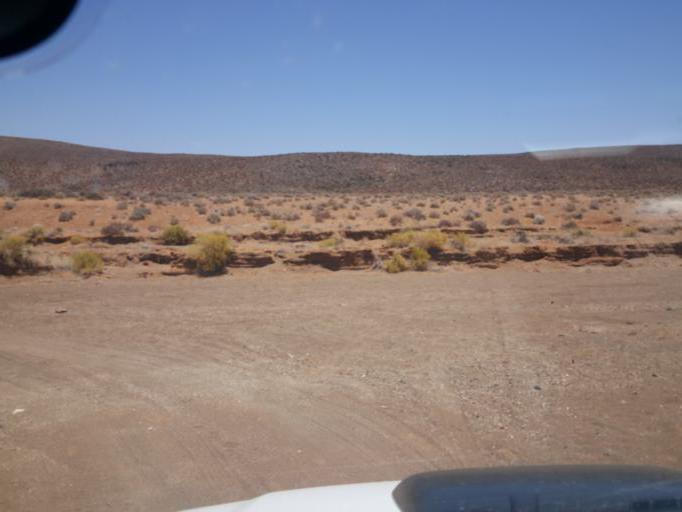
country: ZA
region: Northern Cape
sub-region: Namakwa District Municipality
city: Calvinia
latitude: -32.2086
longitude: 20.0142
